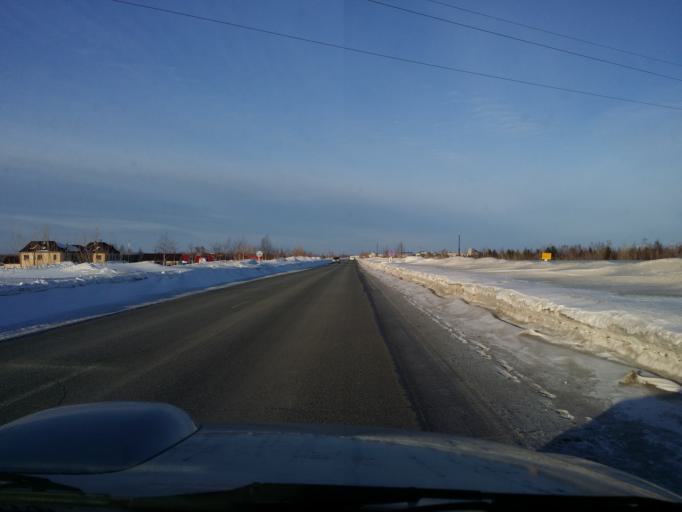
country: RU
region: Khanty-Mansiyskiy Avtonomnyy Okrug
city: Izluchinsk
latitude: 60.9703
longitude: 76.8901
